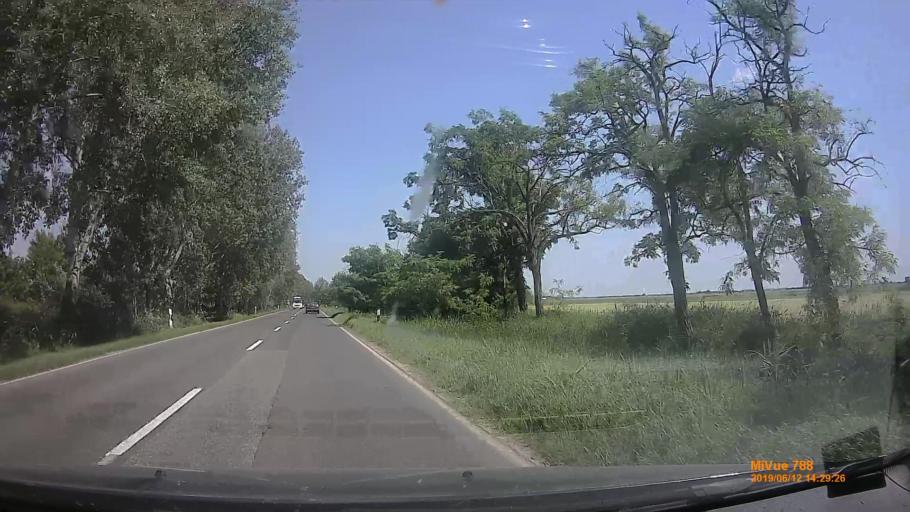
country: HU
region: Csongrad
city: Kiszombor
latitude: 46.2079
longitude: 20.3757
